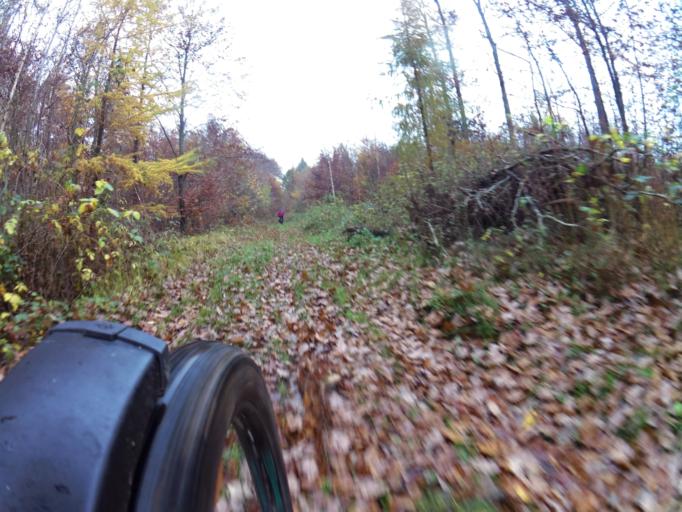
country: PL
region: Pomeranian Voivodeship
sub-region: Powiat pucki
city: Krokowa
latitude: 54.7328
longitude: 18.1315
